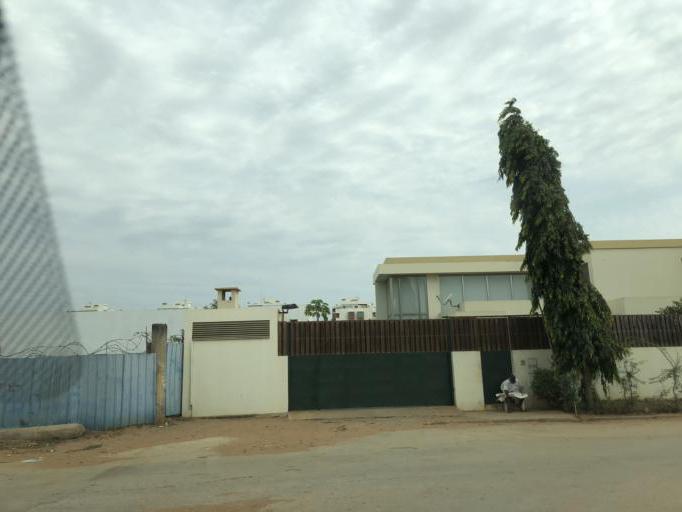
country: AO
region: Luanda
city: Luanda
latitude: -8.8907
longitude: 13.1924
